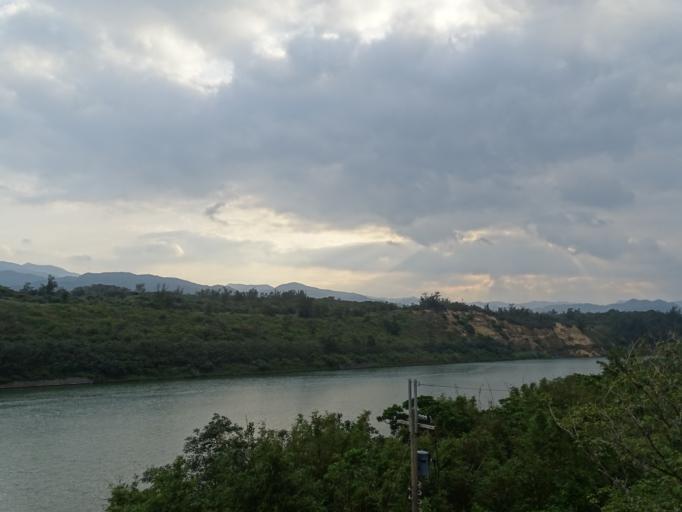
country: TW
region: Taiwan
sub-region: Keelung
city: Keelung
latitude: 25.0237
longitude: 121.9356
